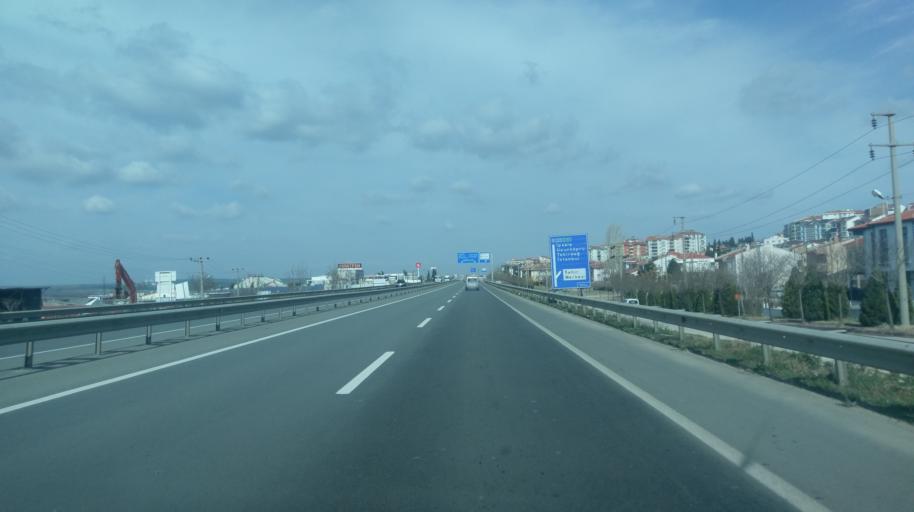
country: TR
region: Edirne
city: Kesan
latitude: 40.8513
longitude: 26.6224
